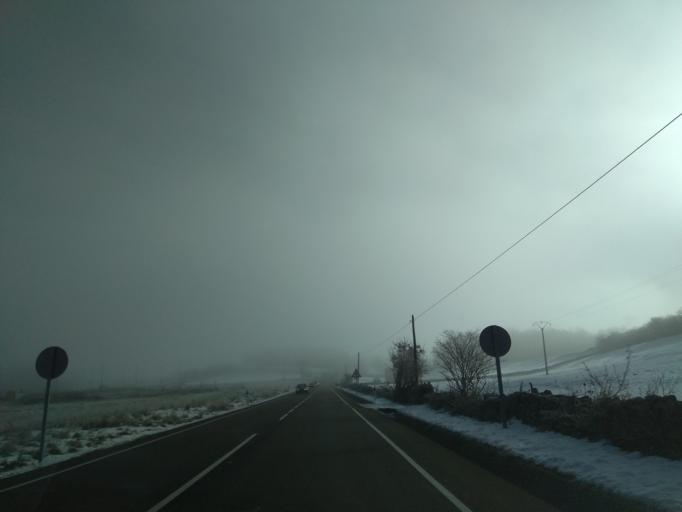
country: ES
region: Castille and Leon
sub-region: Provincia de Burgos
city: Espinosa de los Monteros
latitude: 43.0719
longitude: -3.5302
